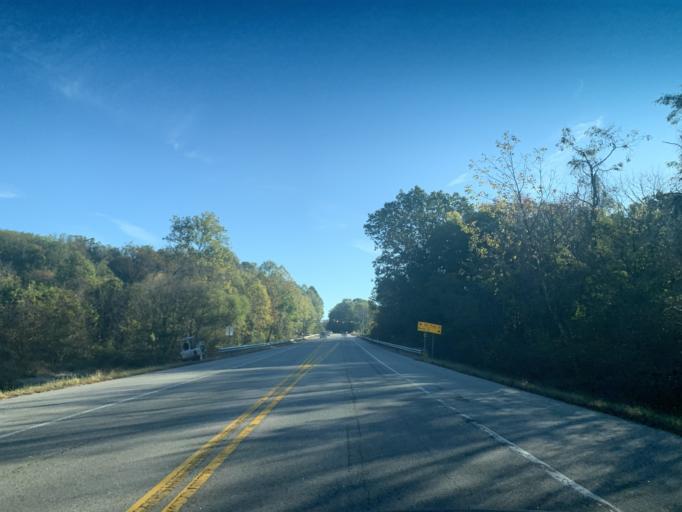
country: US
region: Maryland
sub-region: Cecil County
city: Rising Sun
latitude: 39.7087
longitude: -76.0679
